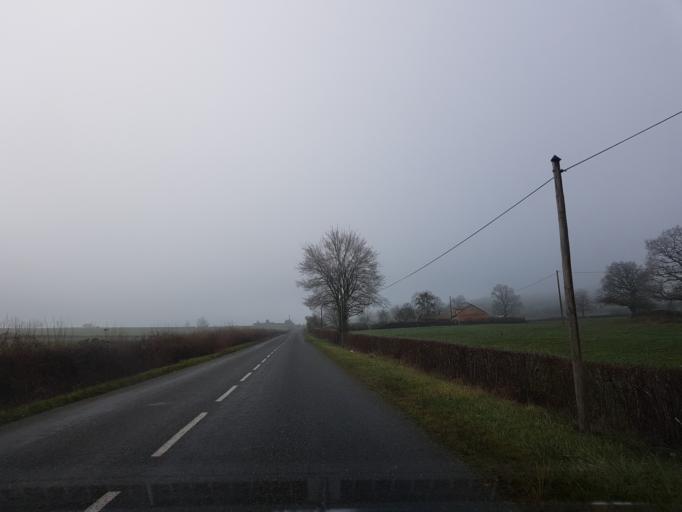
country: FR
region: Bourgogne
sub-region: Departement de Saone-et-Loire
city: Saint-Berain-sous-Sanvignes
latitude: 46.7286
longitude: 4.3061
